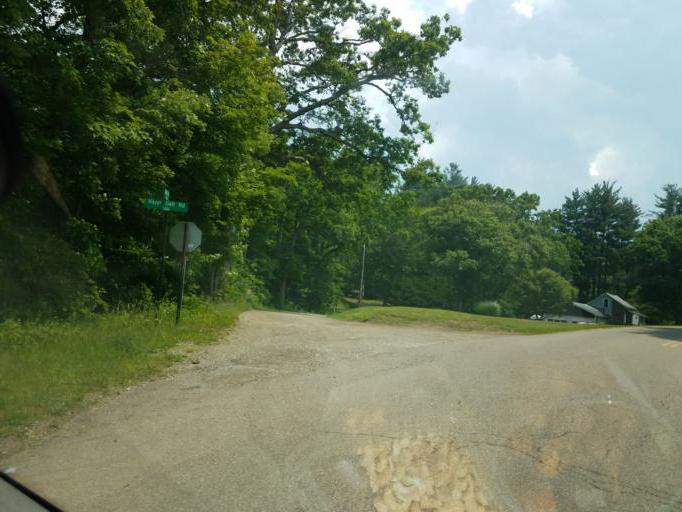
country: US
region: Ohio
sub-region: Knox County
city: Oak Hill
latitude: 40.3827
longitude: -82.2663
